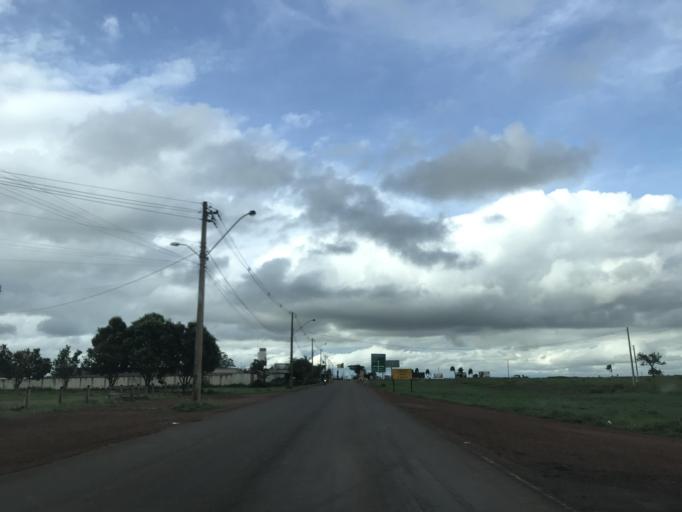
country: BR
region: Goias
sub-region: Vianopolis
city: Vianopolis
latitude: -16.7658
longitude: -48.5220
